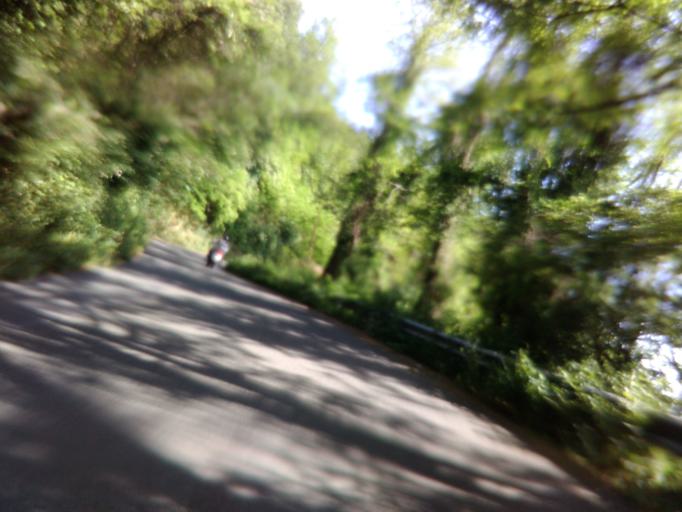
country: IT
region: Tuscany
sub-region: Provincia di Massa-Carrara
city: Fosdinovo
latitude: 44.1188
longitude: 10.0648
